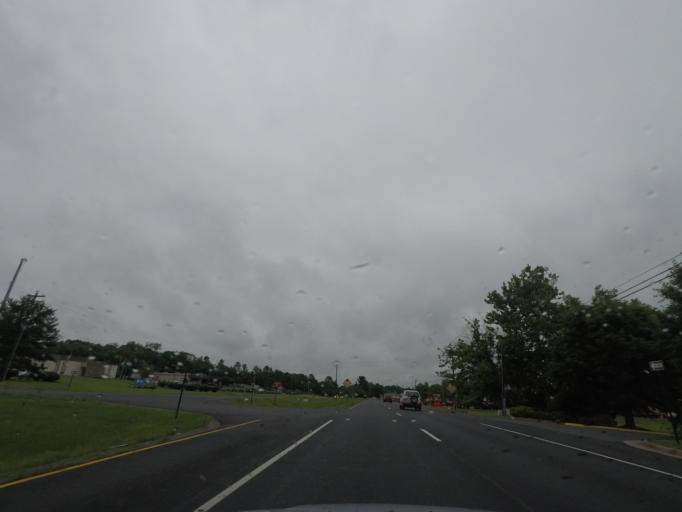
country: US
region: Virginia
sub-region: Orange County
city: Orange
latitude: 38.2284
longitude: -78.1175
